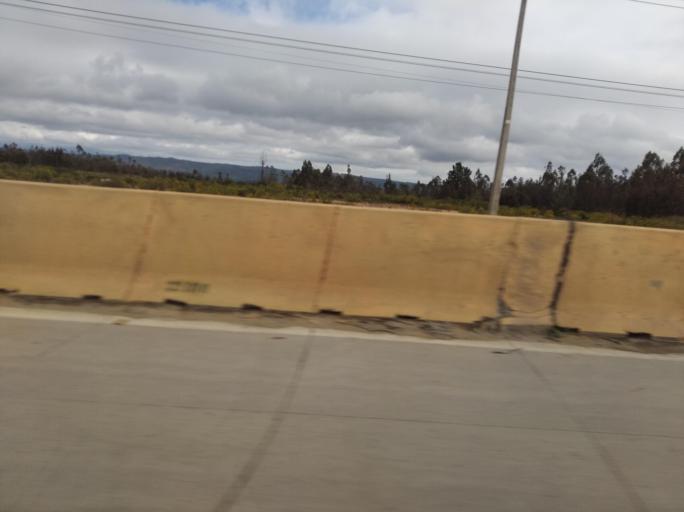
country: CL
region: Valparaiso
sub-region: Provincia de Valparaiso
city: Valparaiso
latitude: -33.0947
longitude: -71.5906
